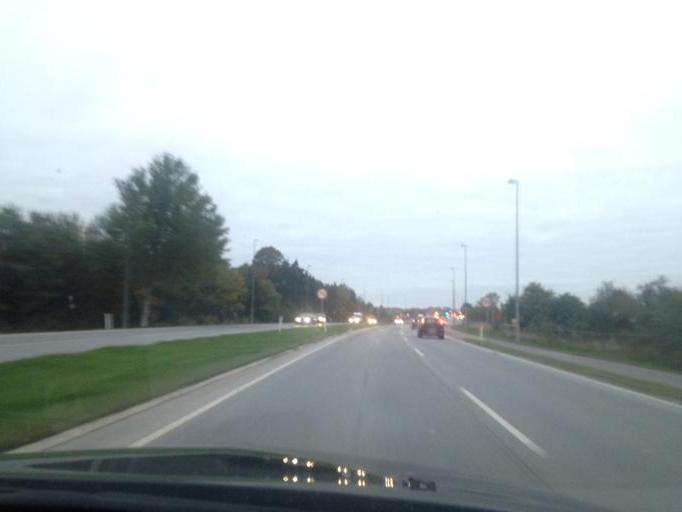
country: DK
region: Zealand
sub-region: Roskilde Kommune
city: Roskilde
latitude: 55.6200
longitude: 12.0932
